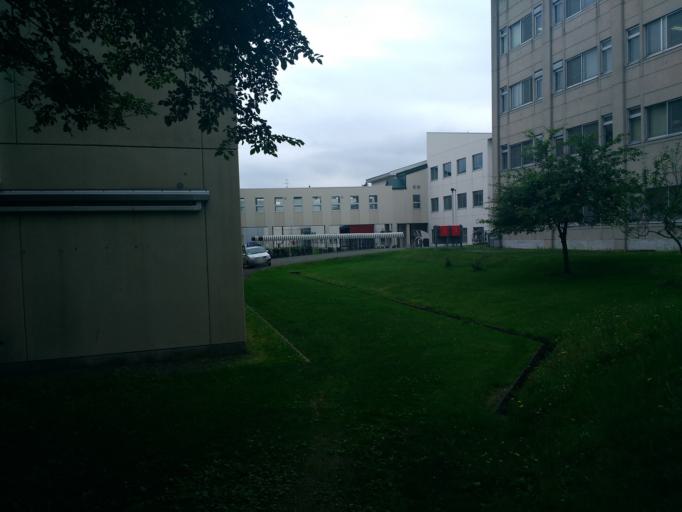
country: JP
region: Hokkaido
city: Ebetsu
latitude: 43.0733
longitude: 141.5110
